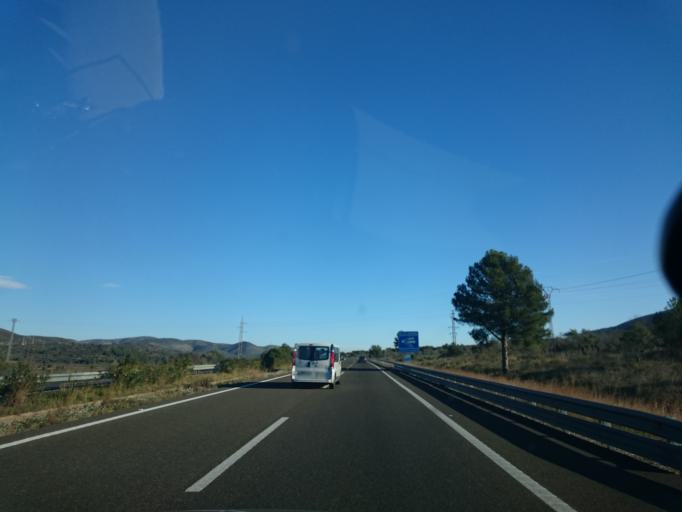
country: ES
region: Valencia
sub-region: Provincia de Castello
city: Alcala de Xivert
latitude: 40.3319
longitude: 0.2626
